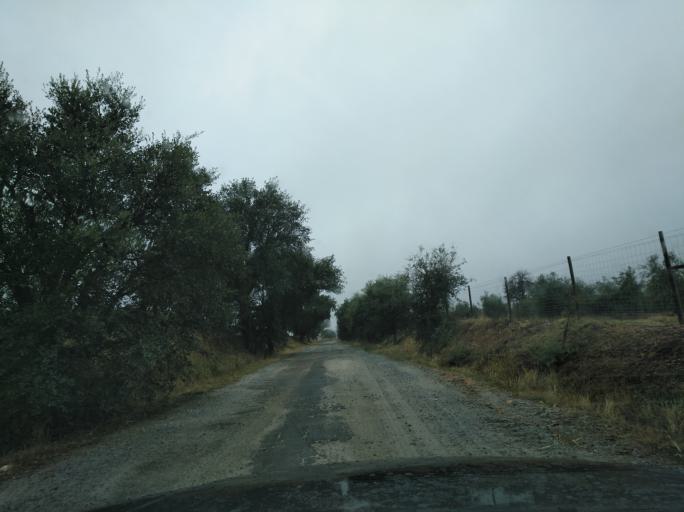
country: PT
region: Portalegre
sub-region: Campo Maior
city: Campo Maior
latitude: 38.9750
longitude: -7.0784
